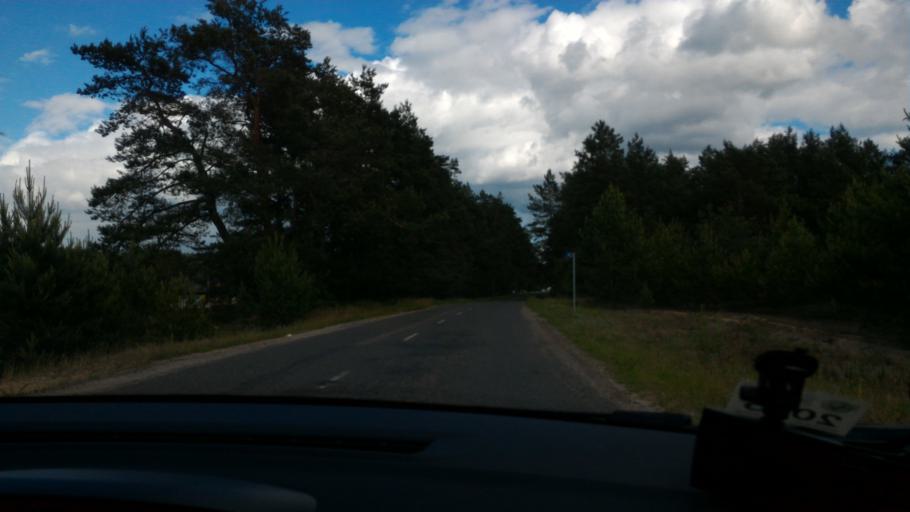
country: BY
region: Brest
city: Ivatsevichy
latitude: 52.7849
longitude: 25.6516
